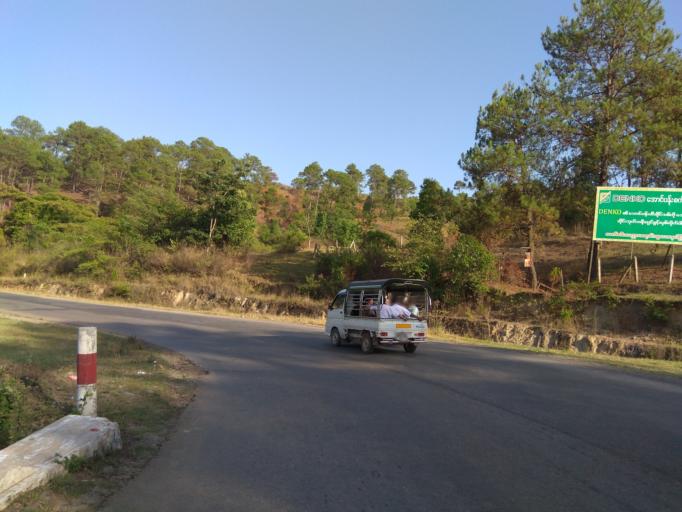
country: MM
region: Shan
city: Taunggyi
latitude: 20.6492
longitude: 96.5953
